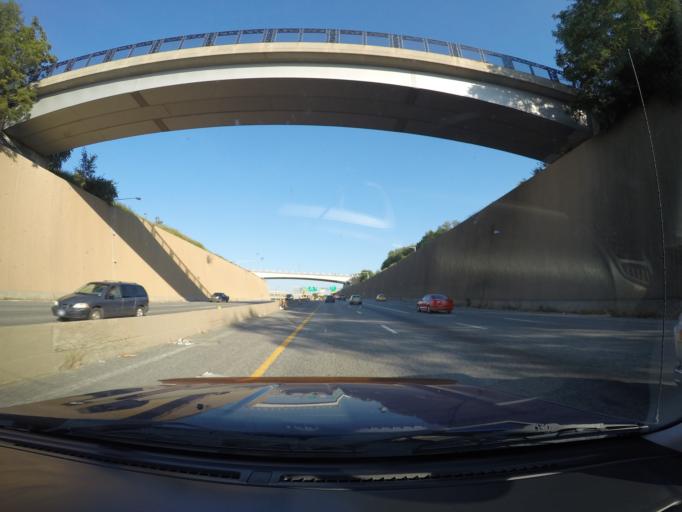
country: US
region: Missouri
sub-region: Jackson County
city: Kansas City
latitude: 39.0969
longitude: -94.5960
